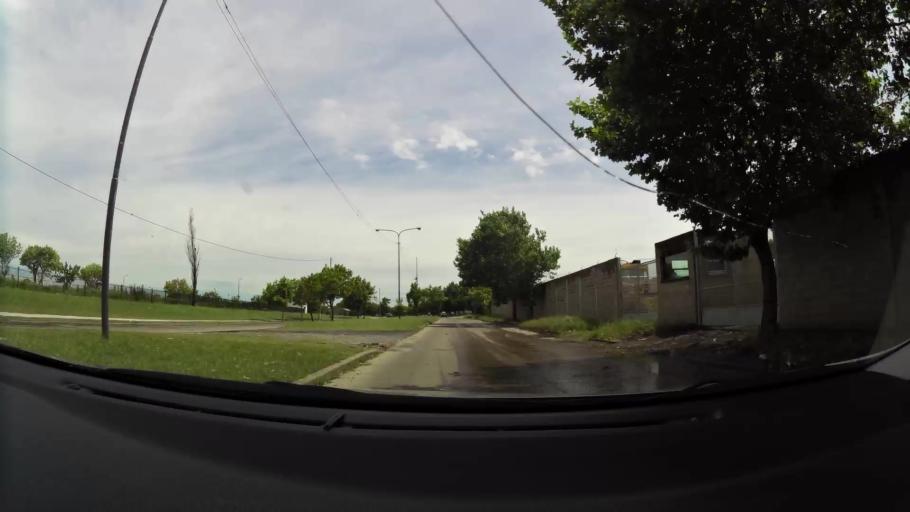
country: AR
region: Buenos Aires F.D.
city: Villa Lugano
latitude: -34.6590
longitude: -58.4631
